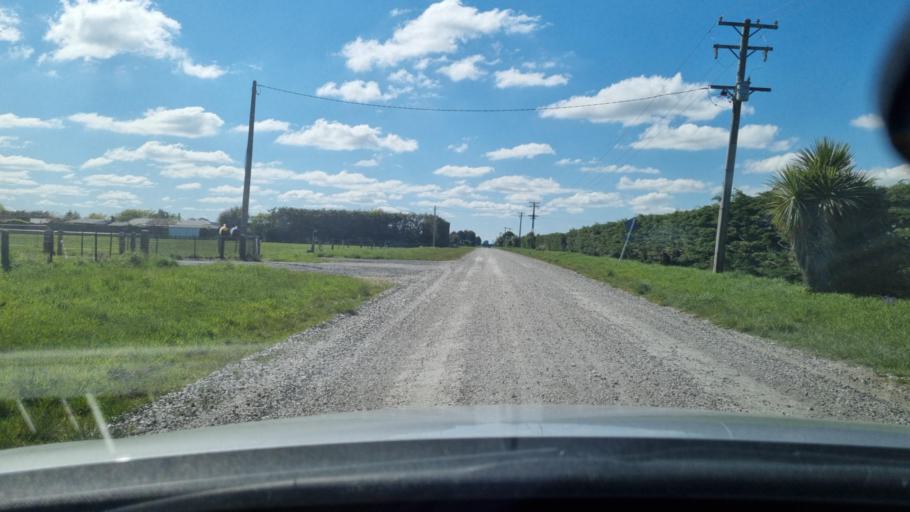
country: NZ
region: Southland
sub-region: Invercargill City
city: Invercargill
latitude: -46.3770
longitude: 168.2984
